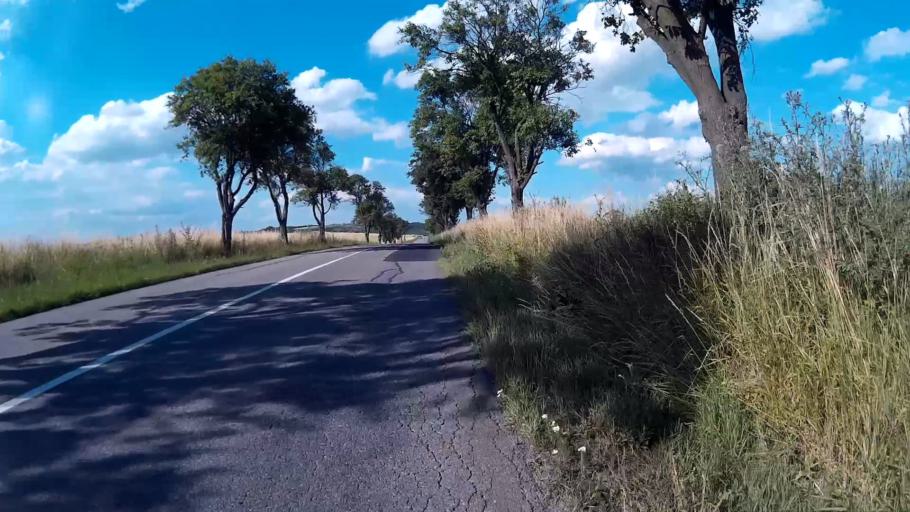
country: CZ
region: South Moravian
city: Sitborice
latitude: 49.0287
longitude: 16.7846
